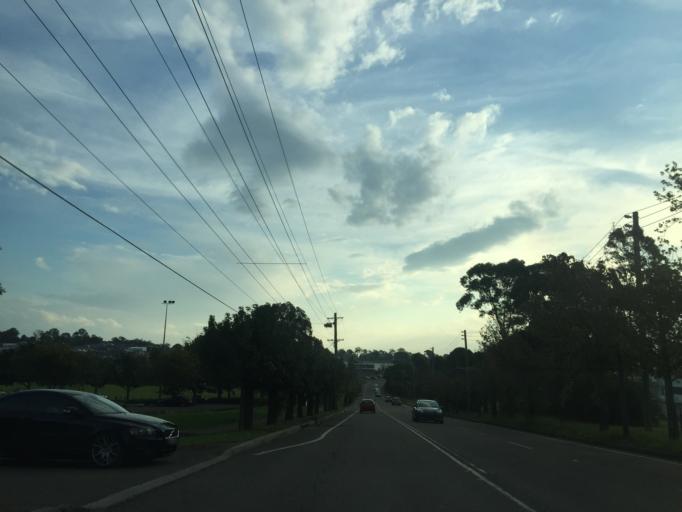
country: AU
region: New South Wales
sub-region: The Hills Shire
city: Beaumont Hills
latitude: -33.7167
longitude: 150.9584
